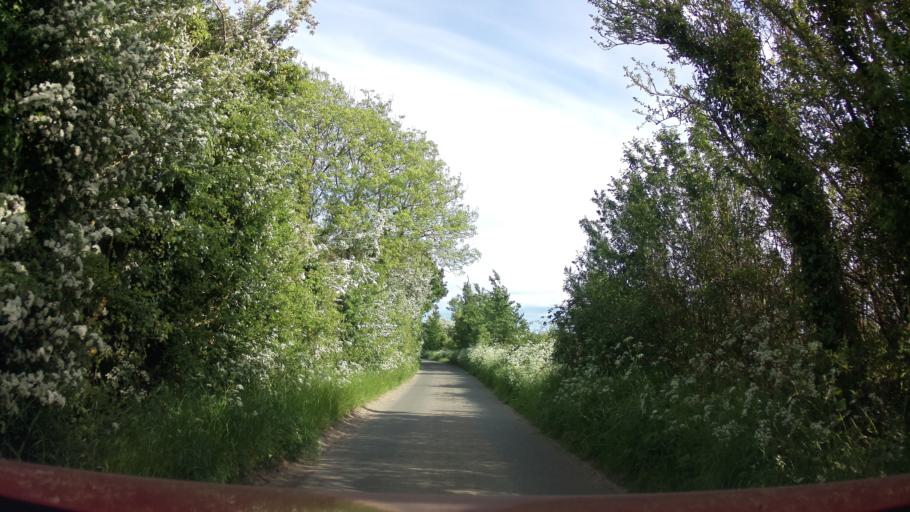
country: GB
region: England
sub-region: Gloucestershire
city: Donnington
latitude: 51.9498
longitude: -1.7821
